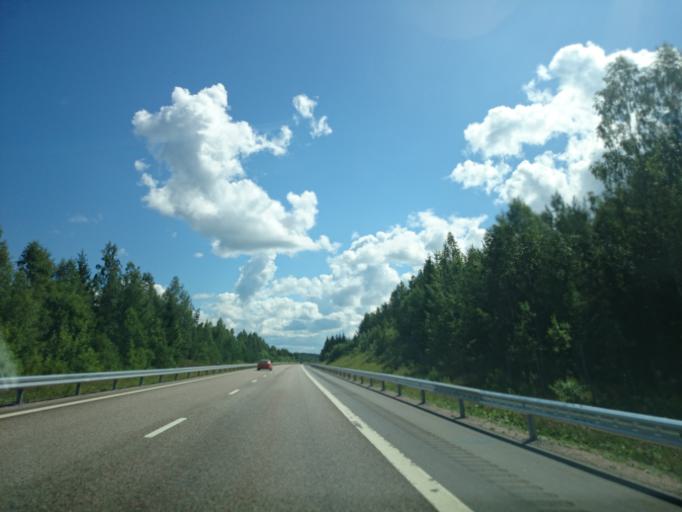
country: SE
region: Uppsala
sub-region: Alvkarleby Kommun
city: AElvkarleby
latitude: 60.4912
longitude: 17.3405
